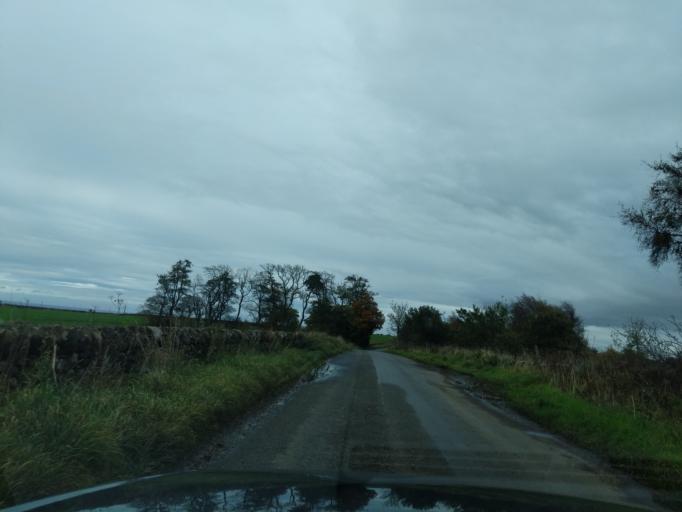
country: GB
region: Scotland
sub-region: Fife
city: Saint Andrews
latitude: 56.2890
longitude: -2.7903
